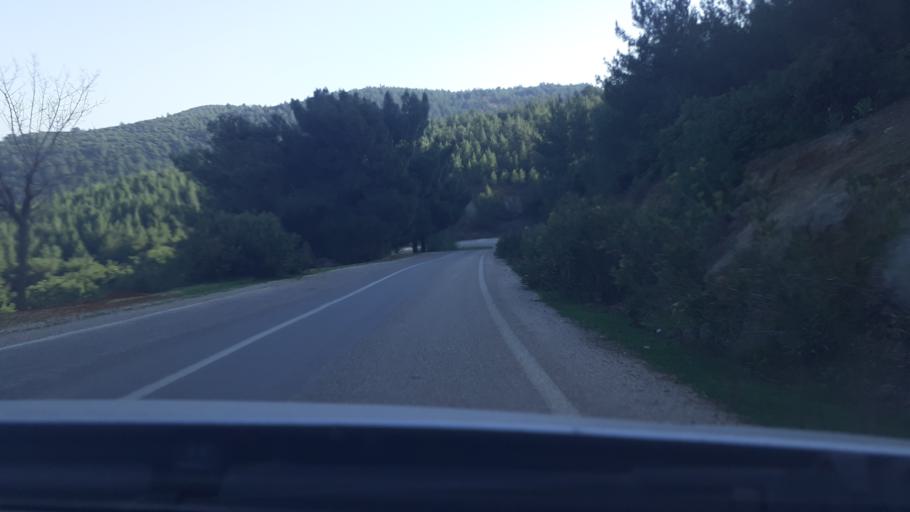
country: TR
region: Hatay
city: Aktepe
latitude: 36.7361
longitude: 36.4652
